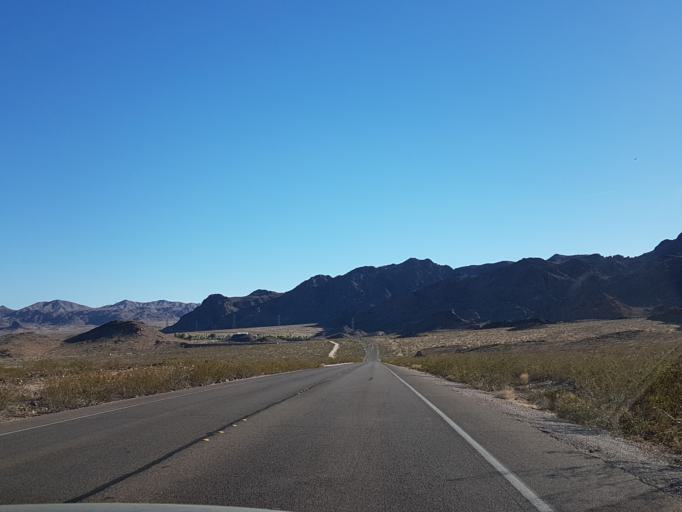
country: US
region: Nevada
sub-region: Clark County
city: Boulder City
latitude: 36.0619
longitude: -114.8200
